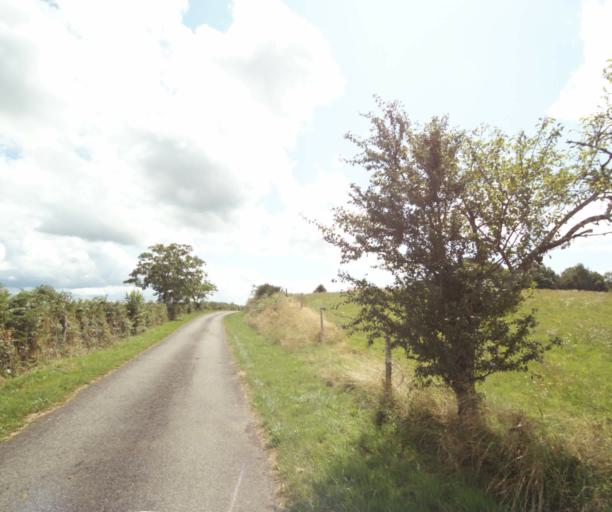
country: FR
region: Limousin
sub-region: Departement de la Correze
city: Sainte-Fortunade
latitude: 45.1752
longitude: 1.8278
